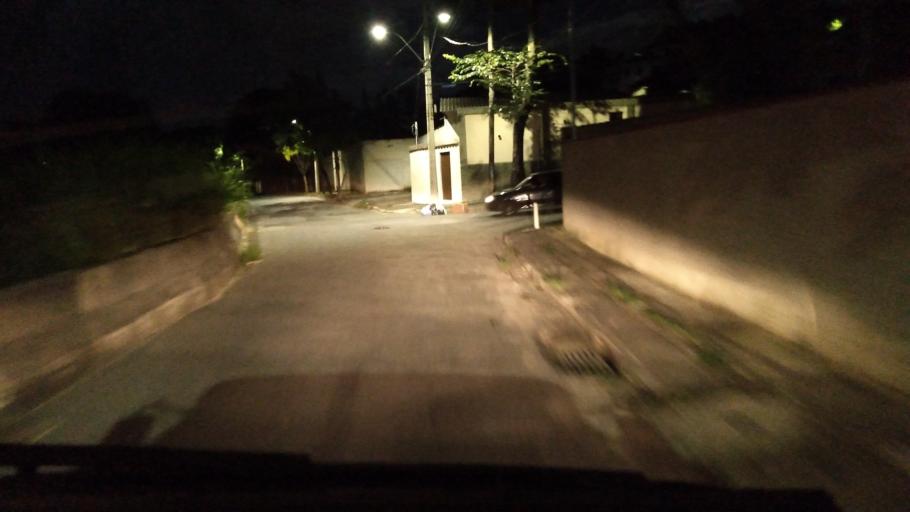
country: BR
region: Minas Gerais
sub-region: Belo Horizonte
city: Belo Horizonte
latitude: -19.8962
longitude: -43.9749
